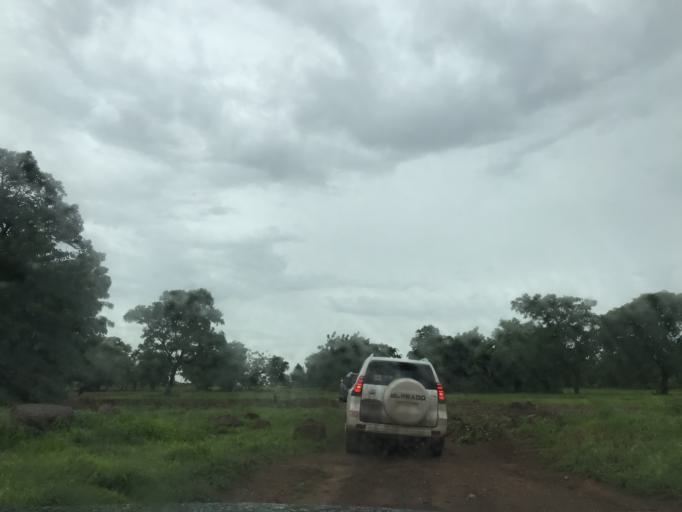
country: GH
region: Upper West
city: Wa
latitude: 10.5132
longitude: -2.7030
